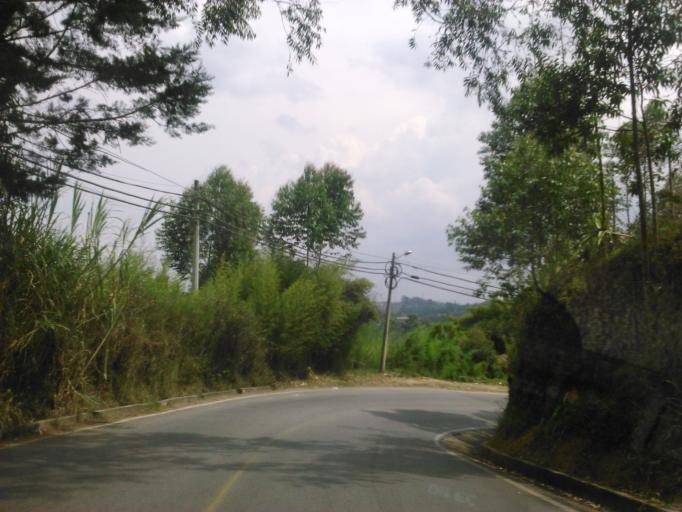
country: CO
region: Antioquia
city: San Vicente
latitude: 6.2252
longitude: -75.3915
